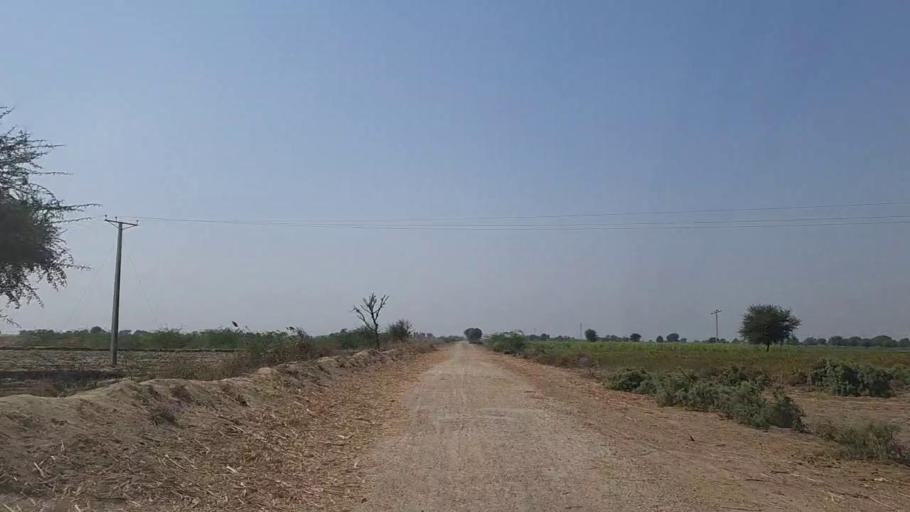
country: PK
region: Sindh
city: Samaro
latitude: 25.2540
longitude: 69.4035
